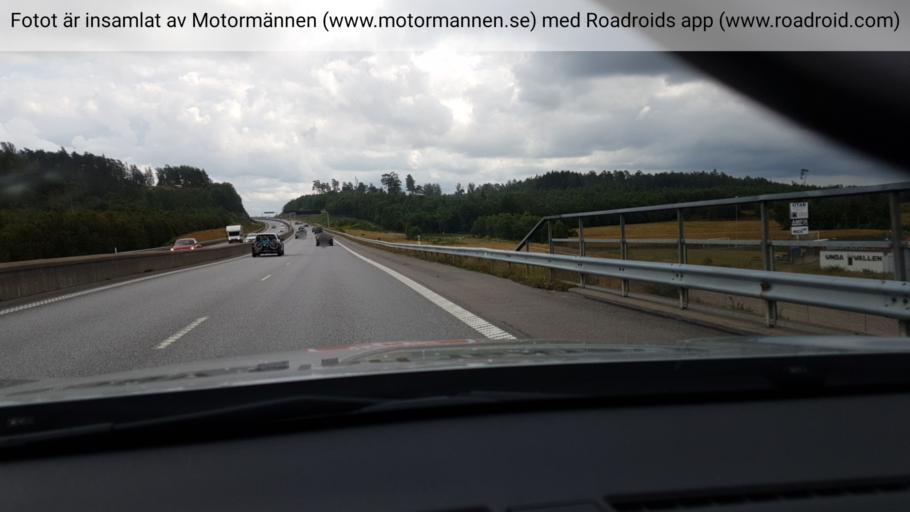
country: SE
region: Vaestra Goetaland
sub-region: Uddevalla Kommun
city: Uddevalla
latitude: 58.3379
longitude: 11.8242
